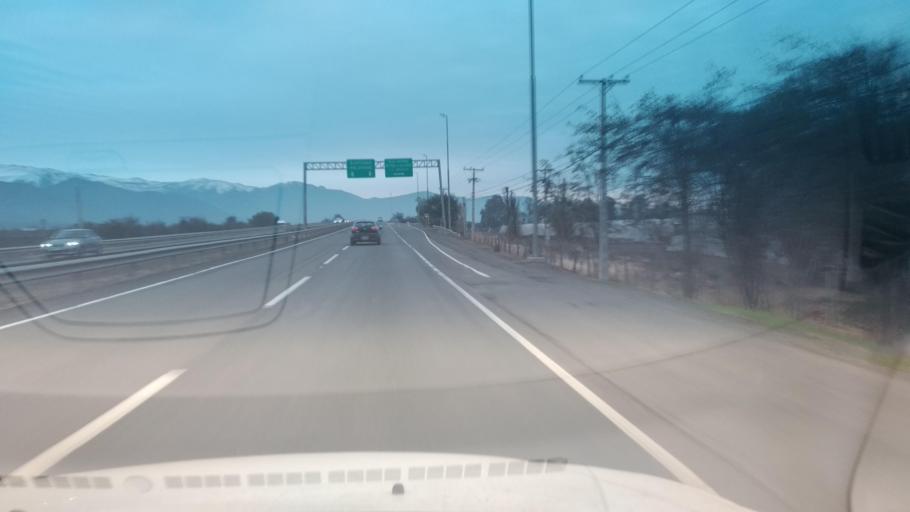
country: CL
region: Santiago Metropolitan
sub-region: Provincia de Chacabuco
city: Chicureo Abajo
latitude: -33.1430
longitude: -70.6609
